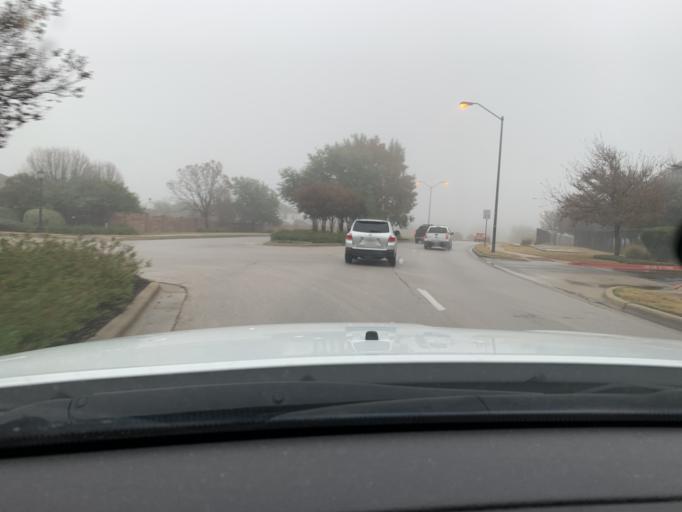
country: US
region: Texas
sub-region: Williamson County
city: Round Rock
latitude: 30.5690
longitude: -97.6856
